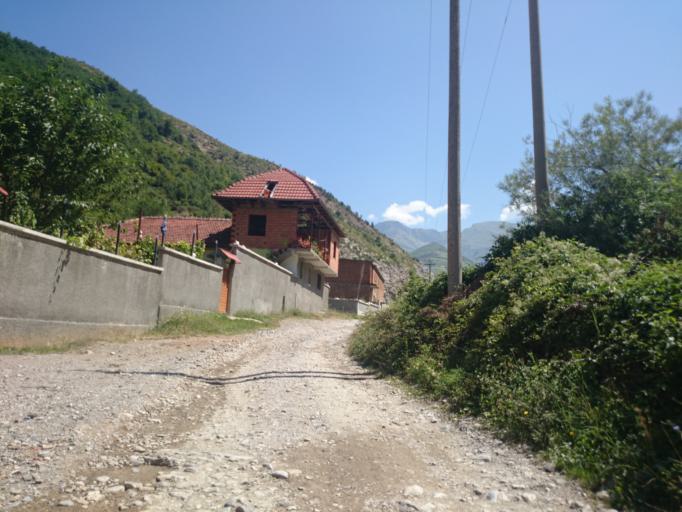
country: AL
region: Diber
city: Peshkopi
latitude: 41.6850
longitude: 20.4530
